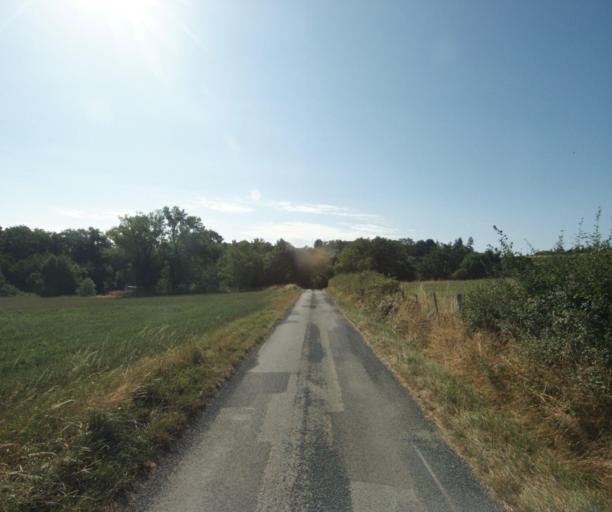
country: FR
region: Rhone-Alpes
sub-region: Departement du Rhone
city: Savigny
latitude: 45.8103
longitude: 4.5819
